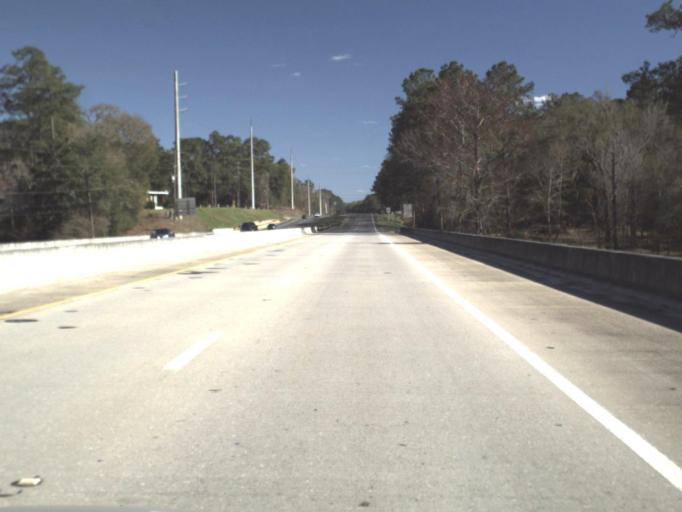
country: US
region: Florida
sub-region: Gadsden County
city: Midway
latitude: 30.4739
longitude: -84.4081
